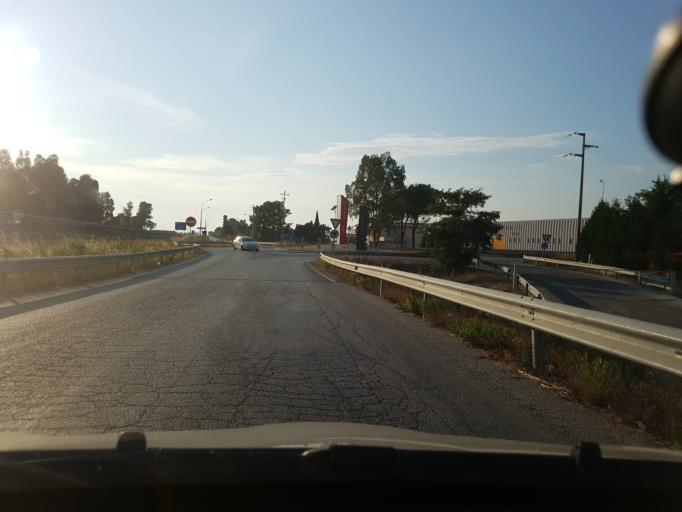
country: IT
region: Apulia
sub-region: Provincia di Foggia
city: Carapelle
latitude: 41.4019
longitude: 15.6505
